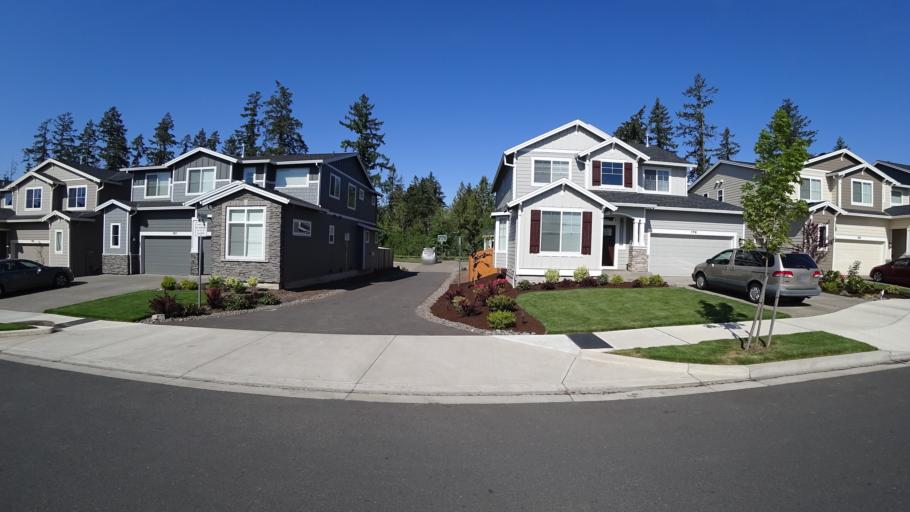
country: US
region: Oregon
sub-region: Washington County
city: Rockcreek
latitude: 45.5216
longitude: -122.9219
